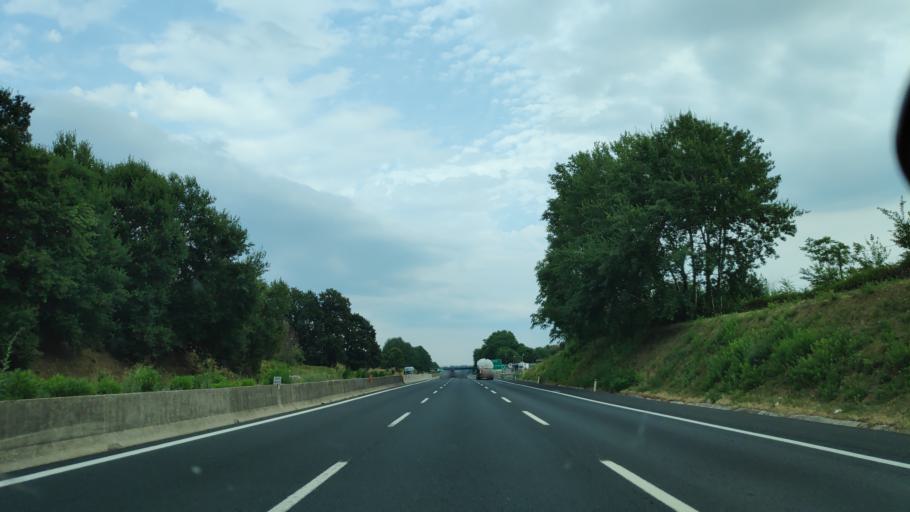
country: IT
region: Latium
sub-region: Provincia di Frosinone
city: Frosinone
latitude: 41.6258
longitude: 13.2947
